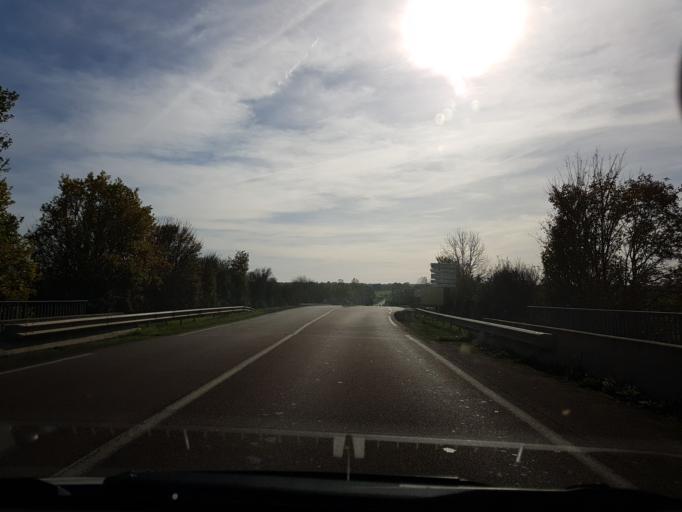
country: FR
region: Bourgogne
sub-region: Departement de l'Yonne
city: Avallon
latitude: 47.5051
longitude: 3.9924
